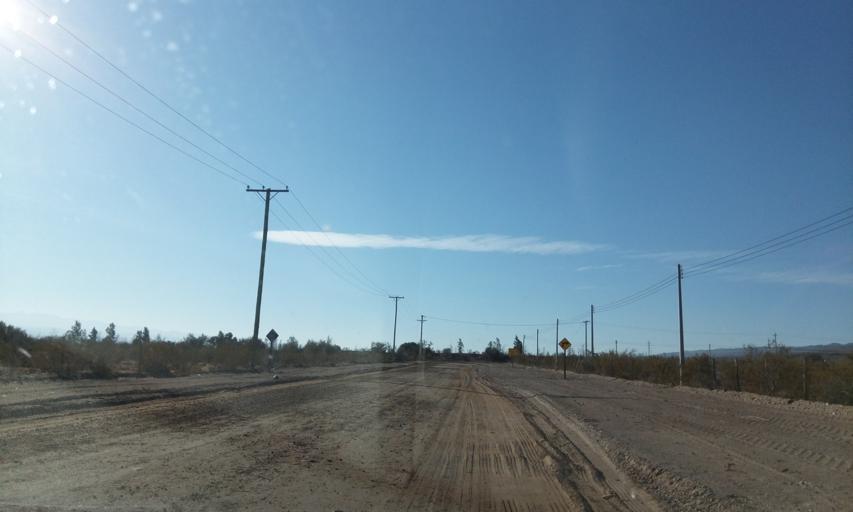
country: AR
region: San Juan
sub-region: Departamento de Rivadavia
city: Rivadavia
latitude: -31.4263
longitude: -68.6719
